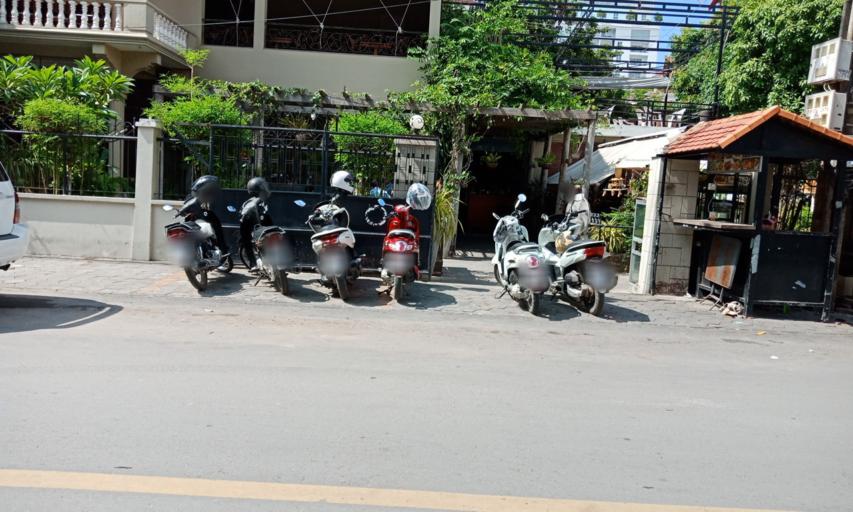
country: KH
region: Phnom Penh
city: Phnom Penh
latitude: 11.5497
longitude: 104.9272
